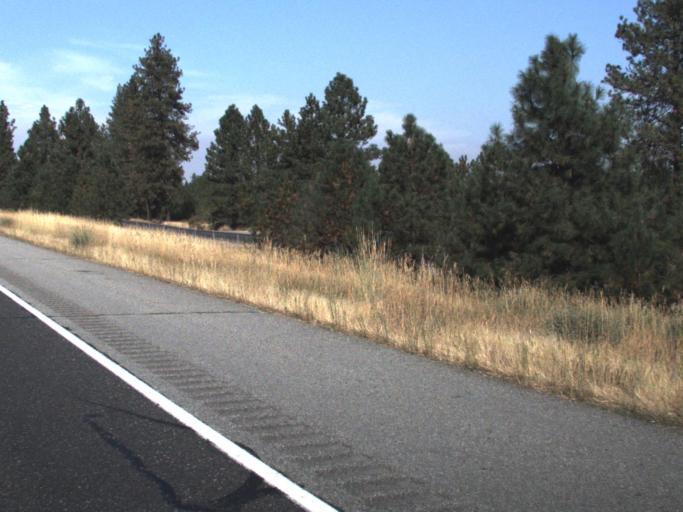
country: US
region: Washington
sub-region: Spokane County
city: Deer Park
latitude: 47.9078
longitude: -117.3505
